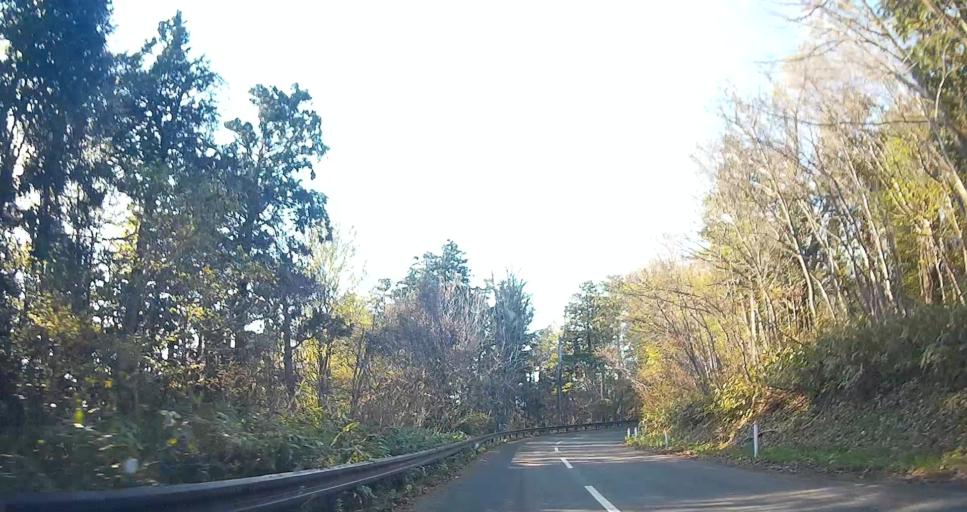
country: JP
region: Aomori
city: Mutsu
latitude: 41.3152
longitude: 141.1085
